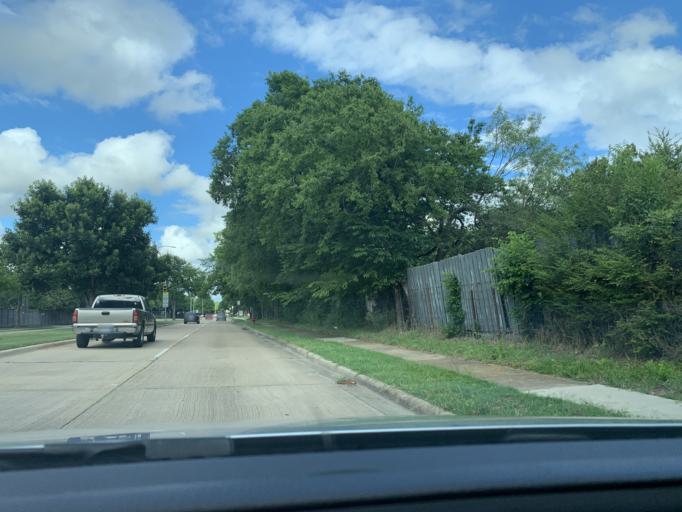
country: US
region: Texas
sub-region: Dallas County
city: Grand Prairie
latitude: 32.6583
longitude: -97.0125
